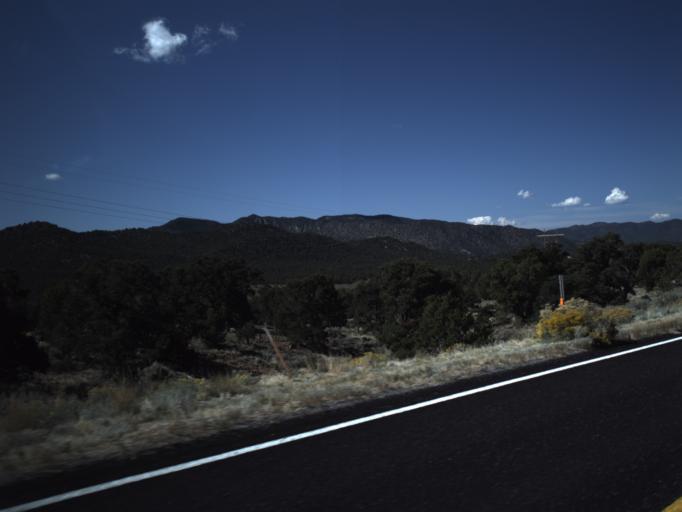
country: US
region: Utah
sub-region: Washington County
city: Enterprise
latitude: 37.6114
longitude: -113.3992
